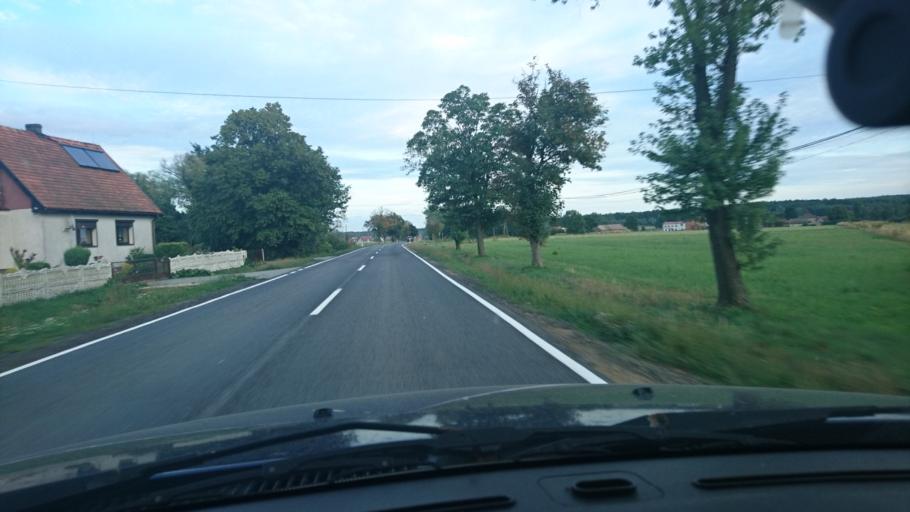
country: PL
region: Silesian Voivodeship
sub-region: Powiat lubliniecki
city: Sierakow Slaski
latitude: 50.8301
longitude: 18.5226
